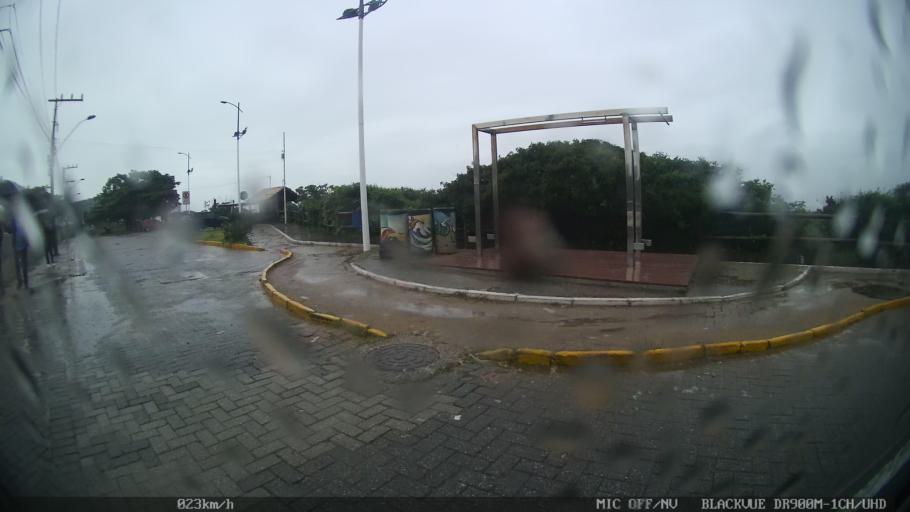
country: BR
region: Santa Catarina
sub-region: Itajai
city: Itajai
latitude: -26.9412
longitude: -48.6287
